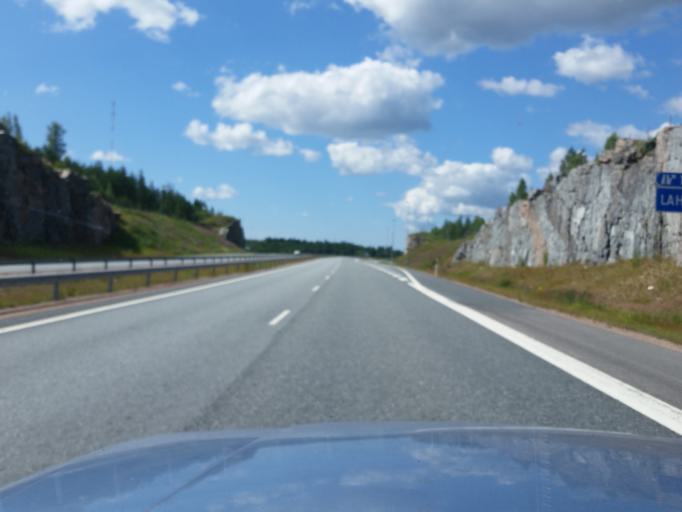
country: FI
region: Varsinais-Suomi
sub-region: Salo
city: Suomusjaervi
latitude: 60.3742
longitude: 23.7167
